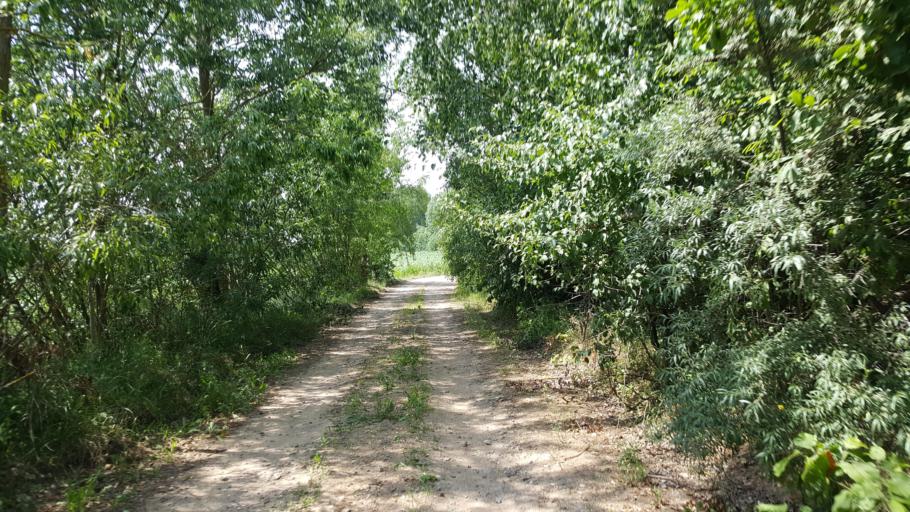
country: BY
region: Brest
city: Kamyanyets
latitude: 52.3651
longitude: 23.7595
